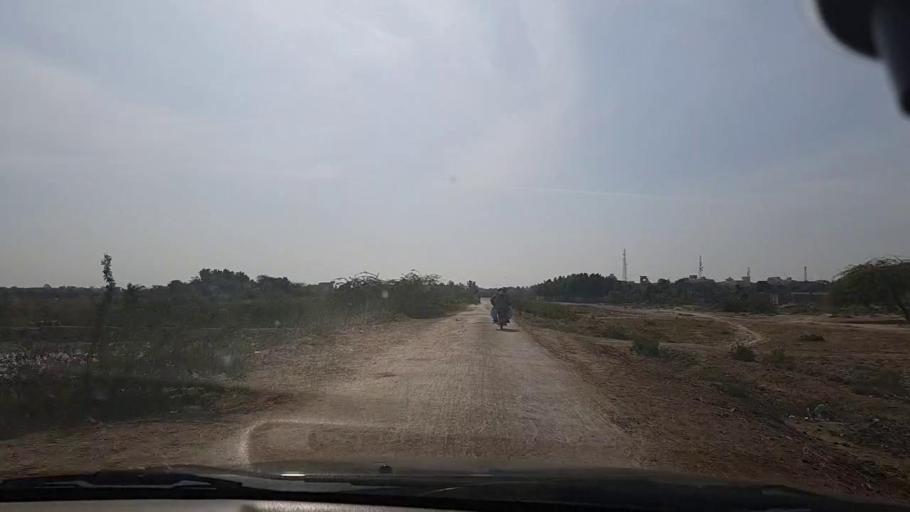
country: PK
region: Sindh
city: Mirpur Batoro
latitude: 24.7349
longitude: 68.2654
